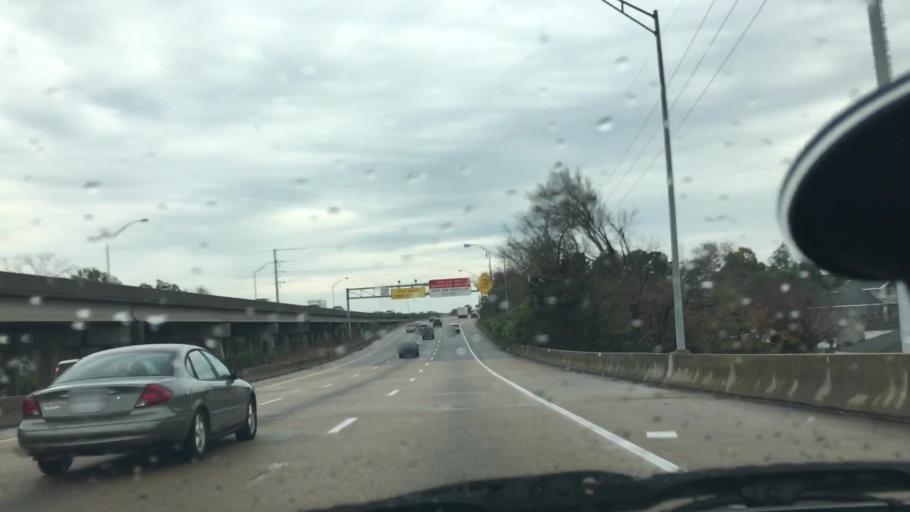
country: US
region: Virginia
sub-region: City of Hampton
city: East Hampton
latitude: 37.0304
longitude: -76.3360
